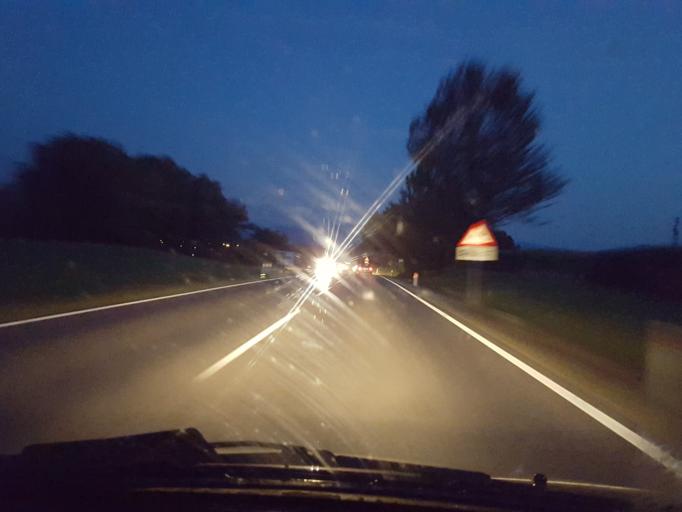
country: AT
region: Lower Austria
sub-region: Politischer Bezirk Scheibbs
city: Wieselburg
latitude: 48.1142
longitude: 15.1366
